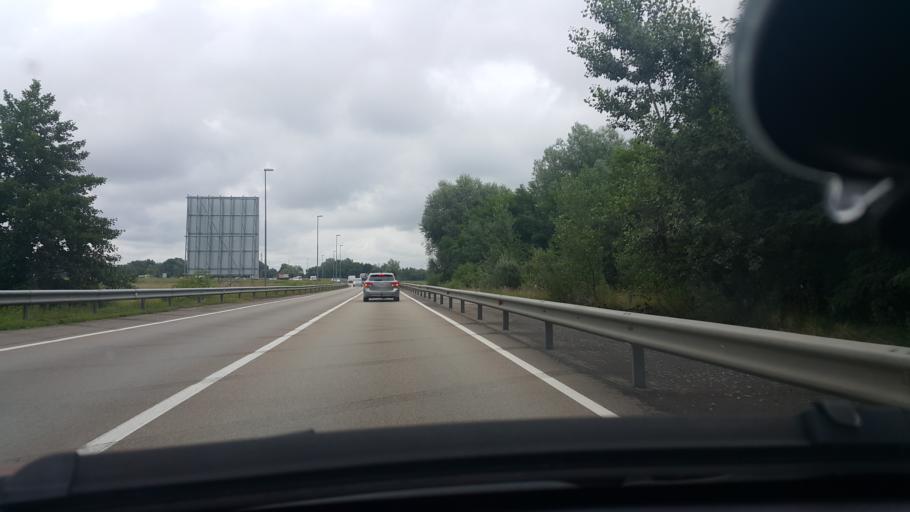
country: SI
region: Ptuj
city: Ptuj
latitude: 46.3978
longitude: 15.8725
